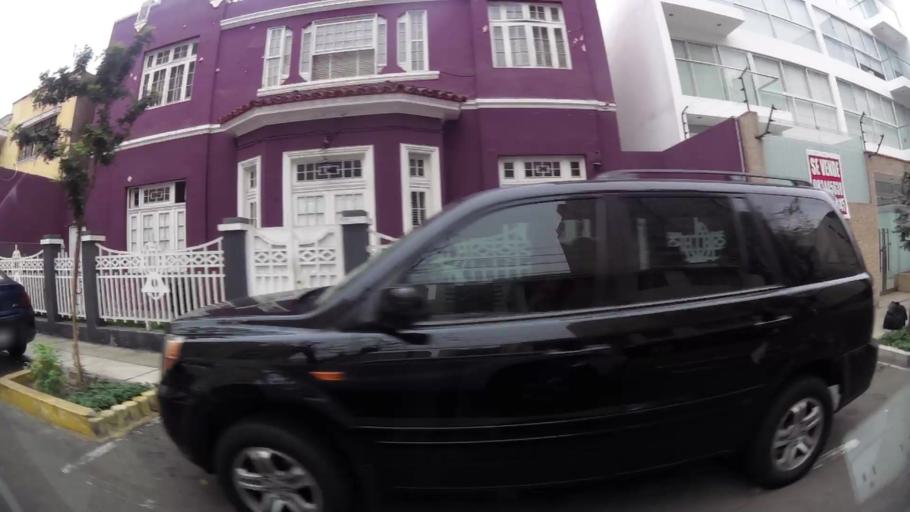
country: PE
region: Lima
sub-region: Lima
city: Surco
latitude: -12.1265
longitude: -77.0260
